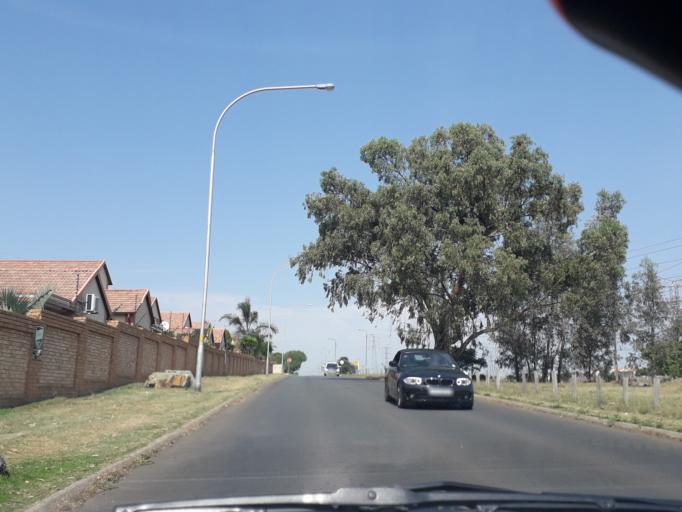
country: ZA
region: Gauteng
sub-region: City of Johannesburg Metropolitan Municipality
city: Modderfontein
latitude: -26.1218
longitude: 28.1659
